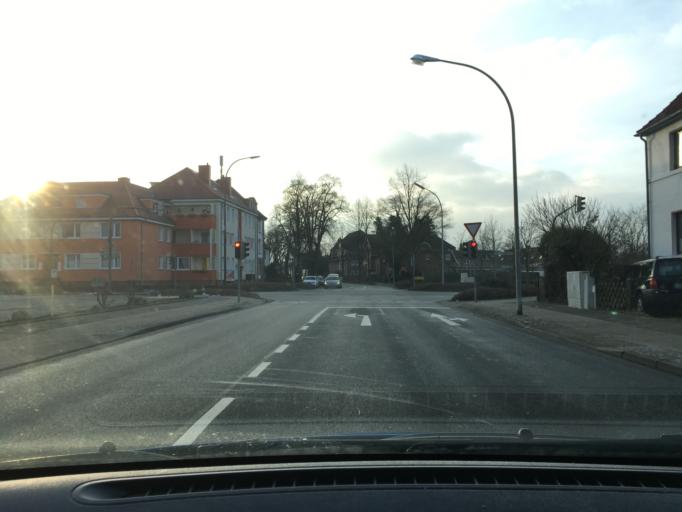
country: DE
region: Lower Saxony
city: Uelzen
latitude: 52.9675
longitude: 10.5748
